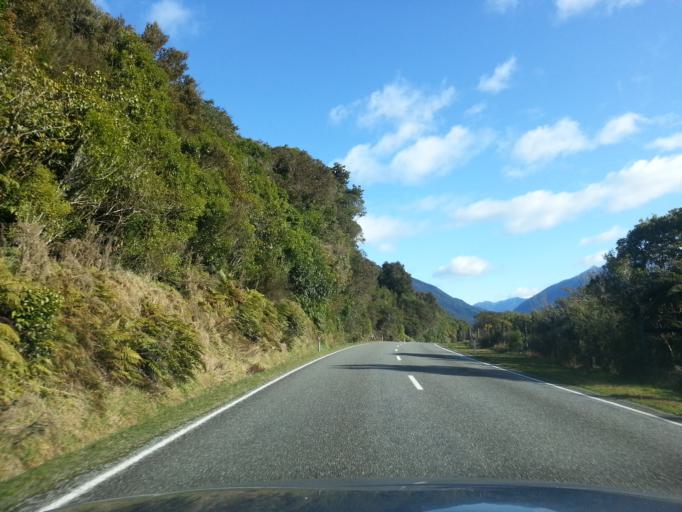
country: NZ
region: West Coast
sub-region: Grey District
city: Greymouth
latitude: -42.7406
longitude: 171.4274
